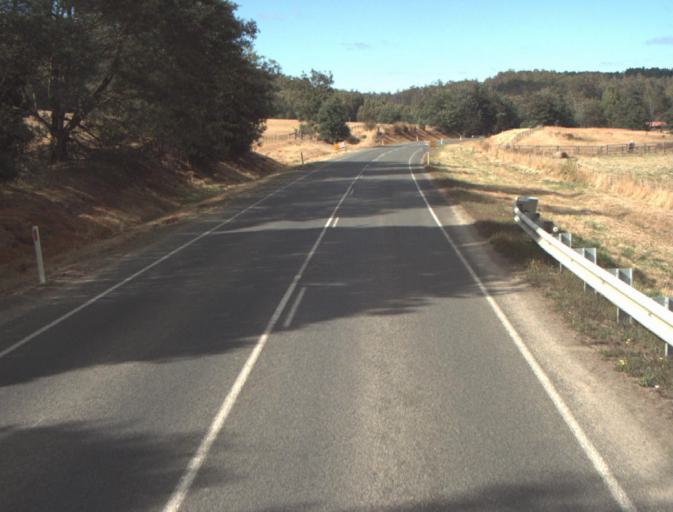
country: AU
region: Tasmania
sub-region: Launceston
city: Mayfield
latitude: -41.2892
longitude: 147.2174
